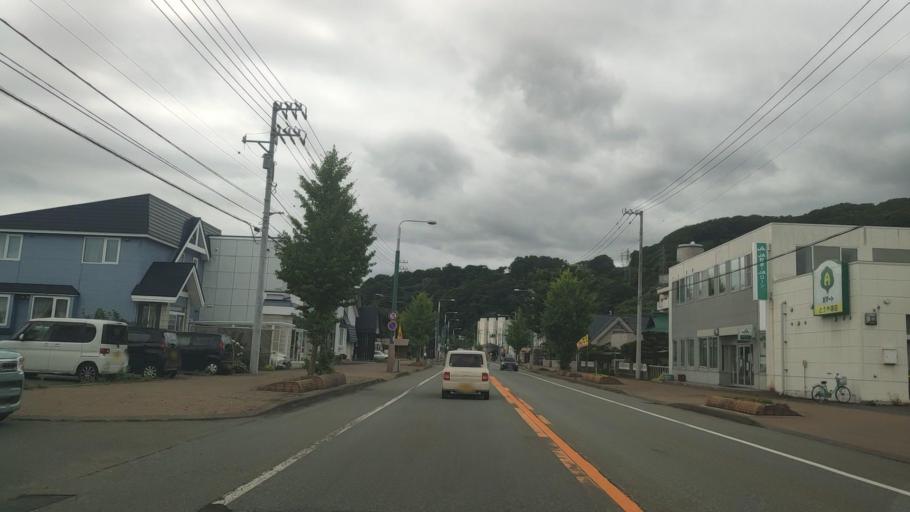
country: JP
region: Hokkaido
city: Date
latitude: 42.5510
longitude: 140.7622
